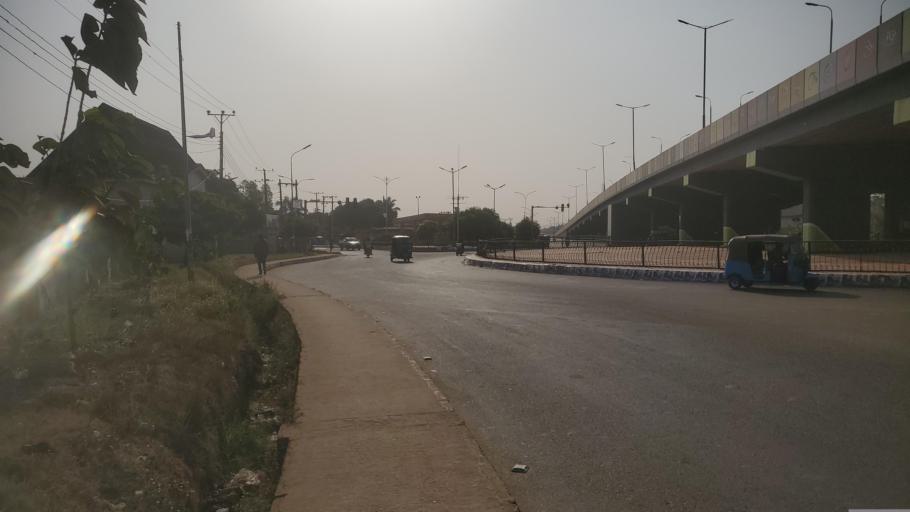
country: NG
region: Ebonyi
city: Abakaliki
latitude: 6.3263
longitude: 8.0836
